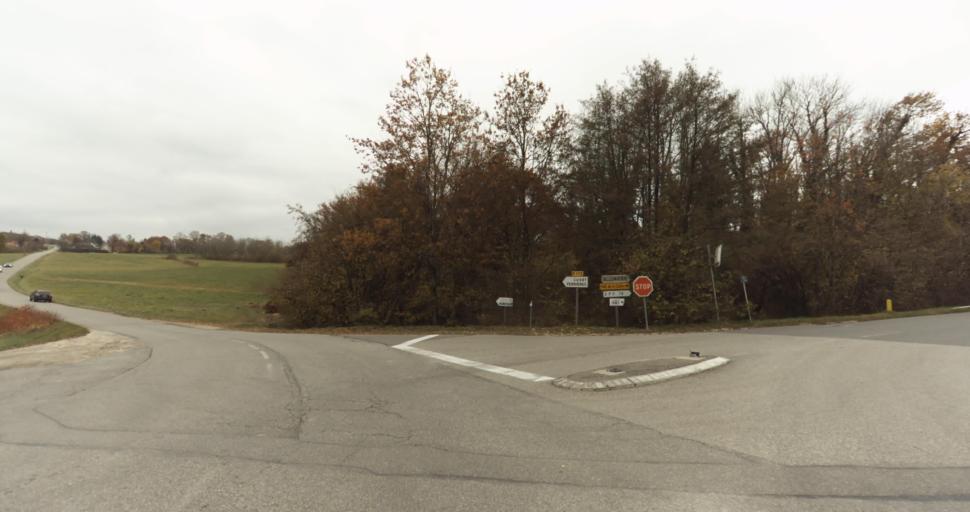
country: FR
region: Rhone-Alpes
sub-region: Departement de la Haute-Savoie
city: Allonzier-la-Caille
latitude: 45.9837
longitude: 6.1272
